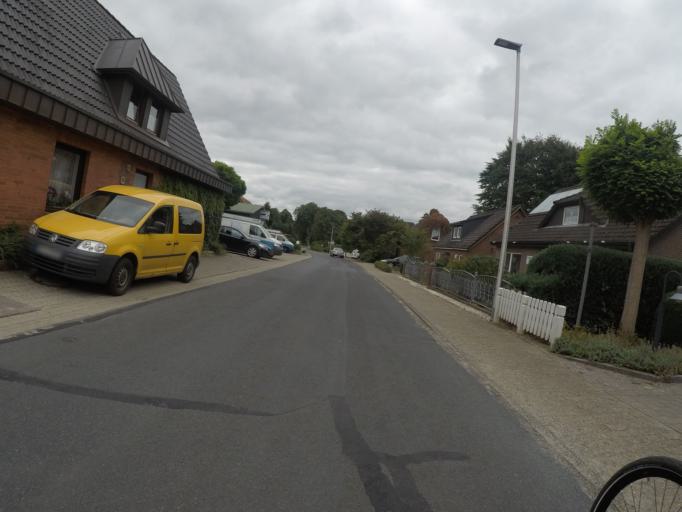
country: DE
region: Lower Saxony
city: Hemmoor
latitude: 53.6966
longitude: 9.1229
